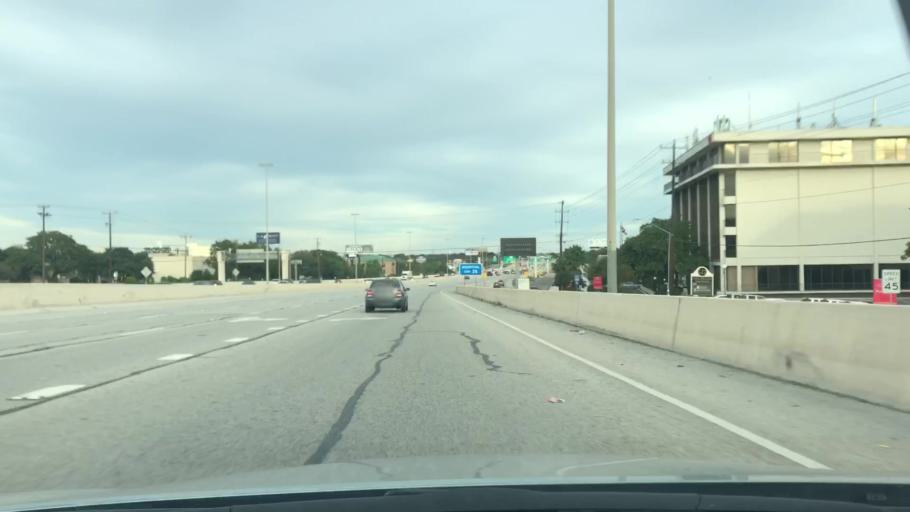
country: US
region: Texas
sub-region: Bexar County
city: Alamo Heights
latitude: 29.5155
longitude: -98.4364
